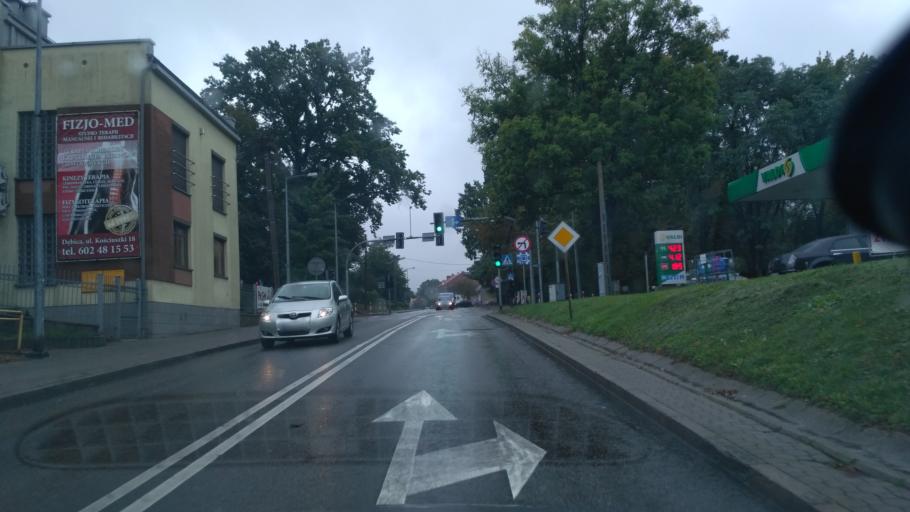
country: PL
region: Subcarpathian Voivodeship
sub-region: Powiat debicki
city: Debica
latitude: 50.0550
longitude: 21.4099
